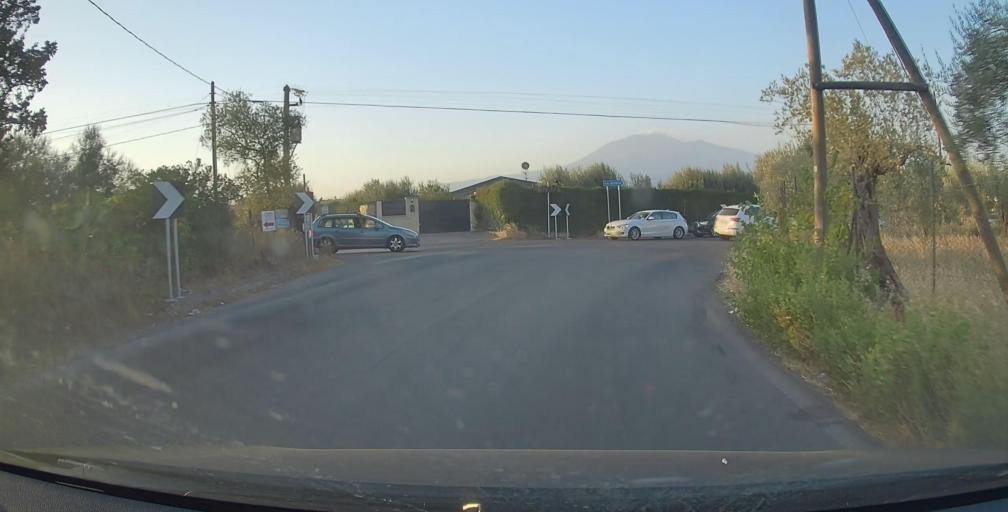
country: IT
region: Sicily
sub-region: Catania
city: Palazzolo
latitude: 37.5461
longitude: 14.9304
